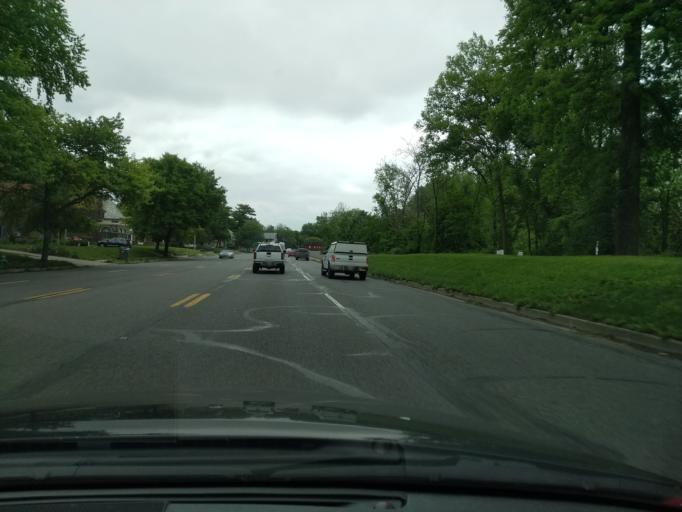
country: US
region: Indiana
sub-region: Marion County
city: Broad Ripple
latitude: 39.8184
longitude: -86.1389
